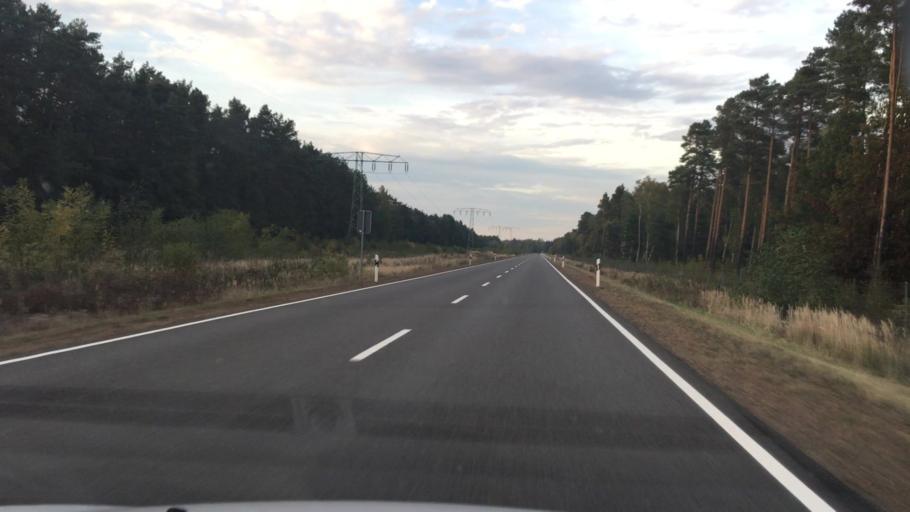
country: DE
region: Brandenburg
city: Schipkau
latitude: 51.5083
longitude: 13.9090
